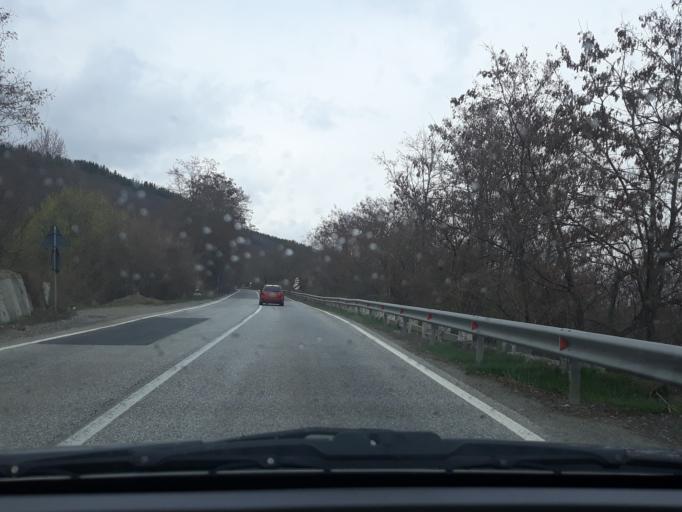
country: RO
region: Harghita
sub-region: Comuna Lupeni
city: Lupeni
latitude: 46.4121
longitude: 25.2225
